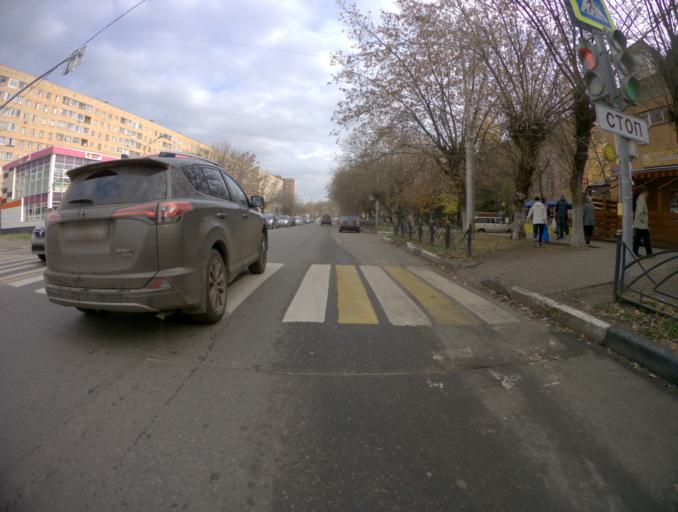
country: RU
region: Moskovskaya
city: Orekhovo-Zuyevo
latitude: 55.7972
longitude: 38.9751
